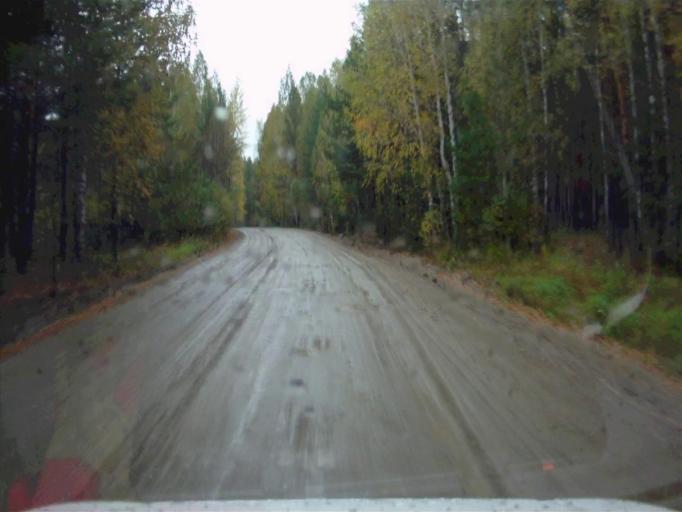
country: RU
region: Chelyabinsk
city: Kyshtym
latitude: 55.7485
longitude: 60.4890
